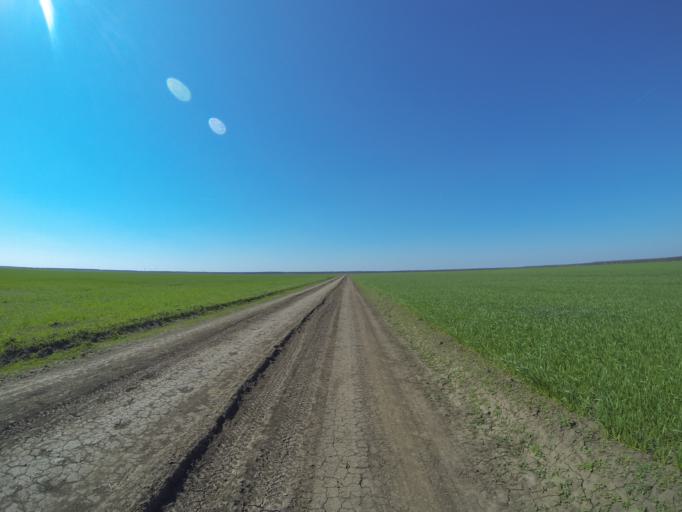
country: RO
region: Dolj
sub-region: Comuna Caloparu
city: Salcuta
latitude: 44.1697
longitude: 23.6648
